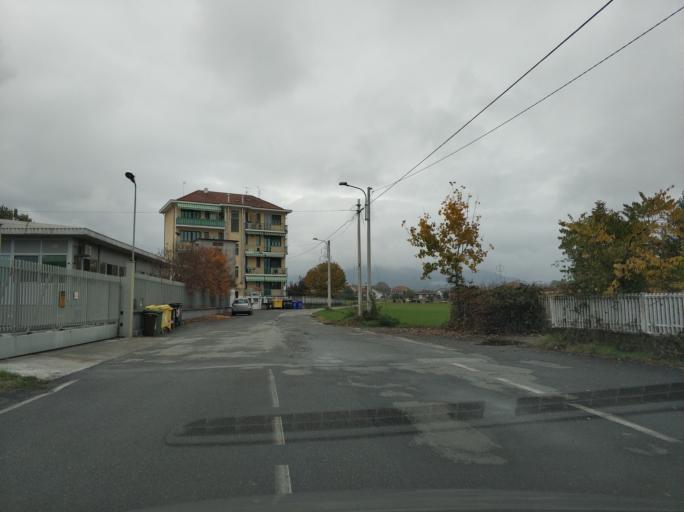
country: IT
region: Piedmont
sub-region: Provincia di Torino
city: Villanova Canavese
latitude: 45.2479
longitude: 7.5513
